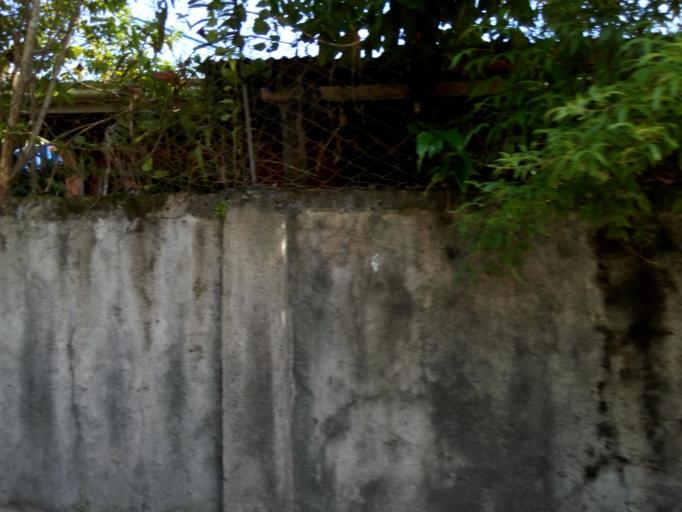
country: PH
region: Caraga
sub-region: Province of Surigao del Norte
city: Surigao
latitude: 9.7838
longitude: 125.4855
